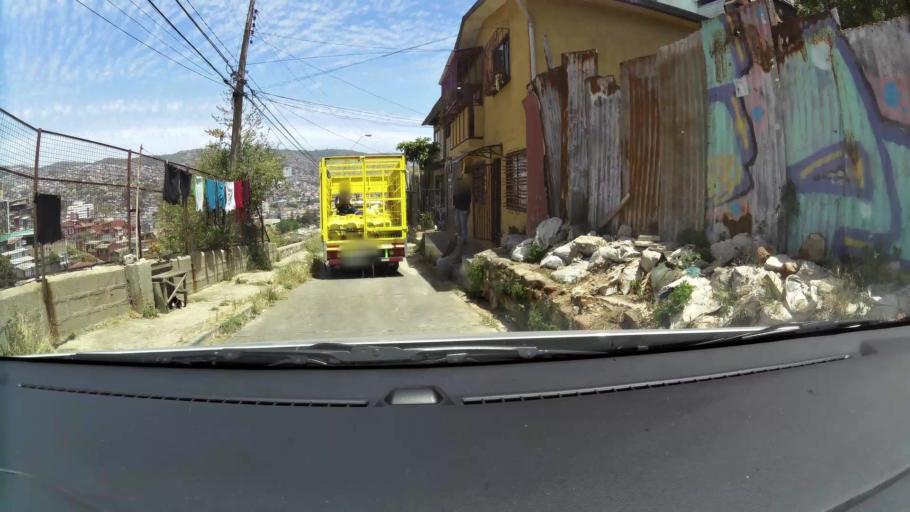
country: CL
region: Valparaiso
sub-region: Provincia de Valparaiso
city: Valparaiso
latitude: -33.0444
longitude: -71.6003
